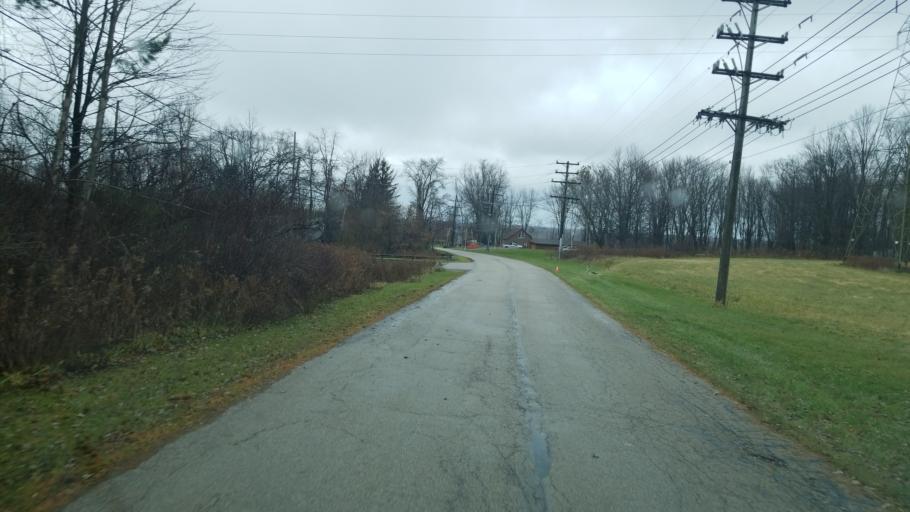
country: US
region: Ohio
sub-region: Ashtabula County
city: Conneaut
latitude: 41.9077
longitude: -80.5717
